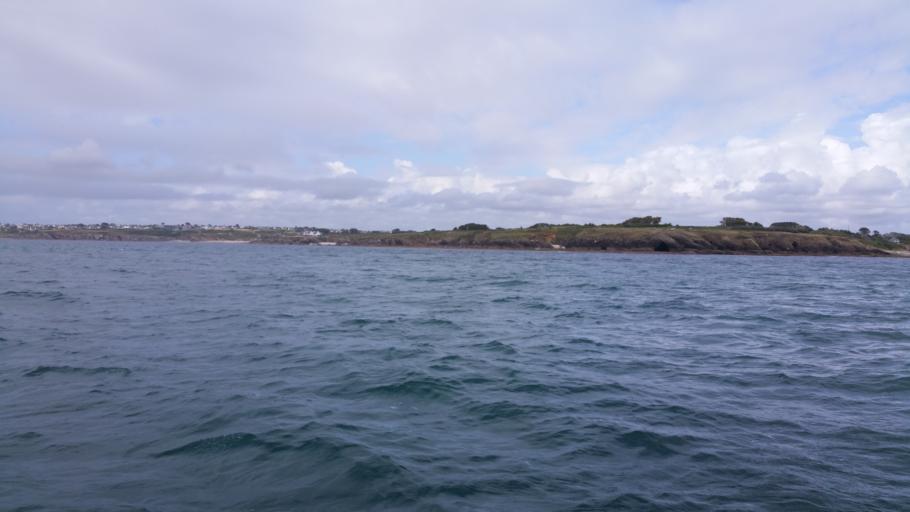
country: FR
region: Brittany
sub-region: Departement du Finistere
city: Le Conquet
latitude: 48.3337
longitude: -4.7823
